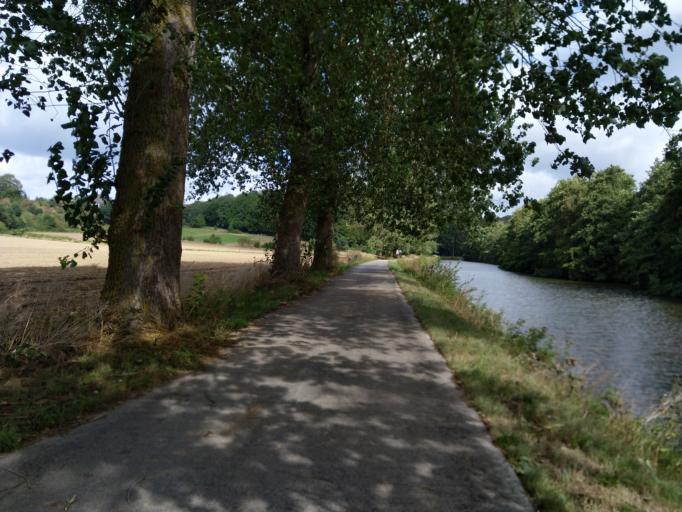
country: BE
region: Wallonia
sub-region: Province du Hainaut
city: Lobbes
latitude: 50.3452
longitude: 4.2485
